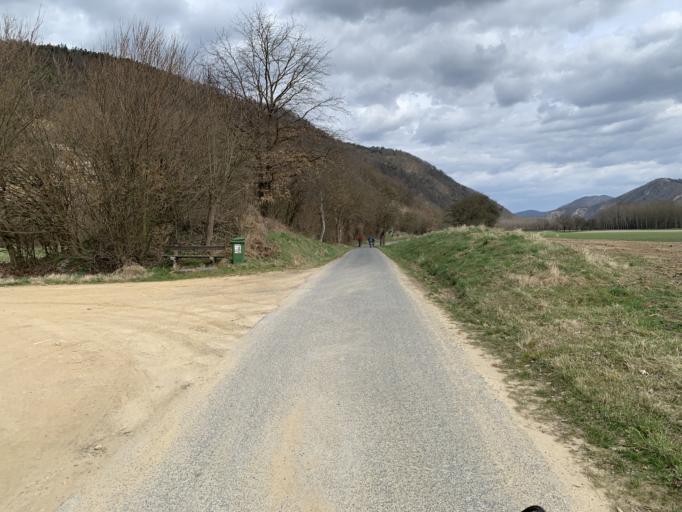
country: AT
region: Lower Austria
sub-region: Politischer Bezirk Melk
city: Emmersdorf an der Donau
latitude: 48.2664
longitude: 15.3683
